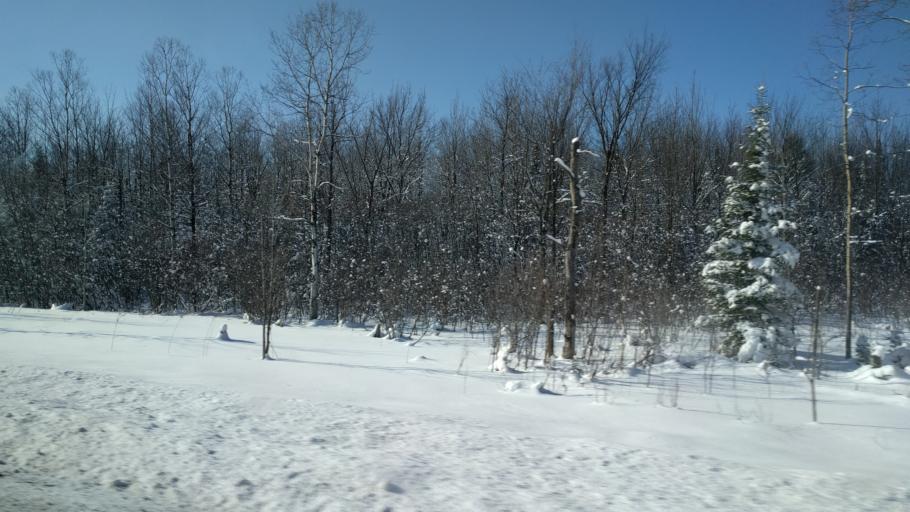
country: US
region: Wisconsin
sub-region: Iron County
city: Hurley
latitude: 46.4013
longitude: -90.3288
